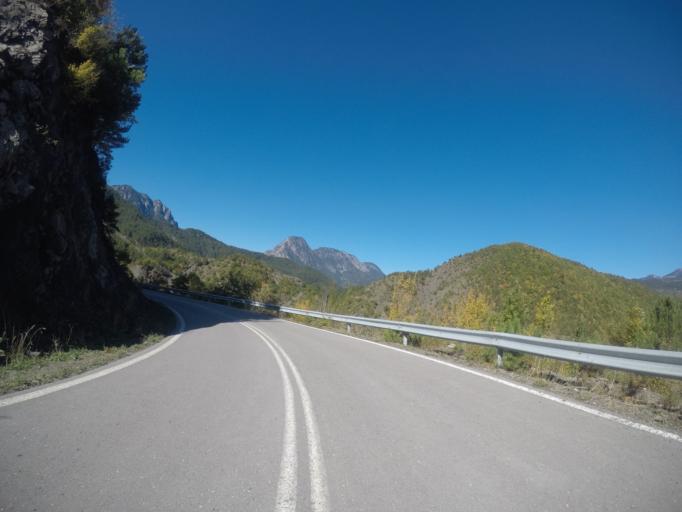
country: GR
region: Epirus
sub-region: Nomos Ioanninon
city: Konitsa
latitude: 40.0116
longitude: 20.8851
